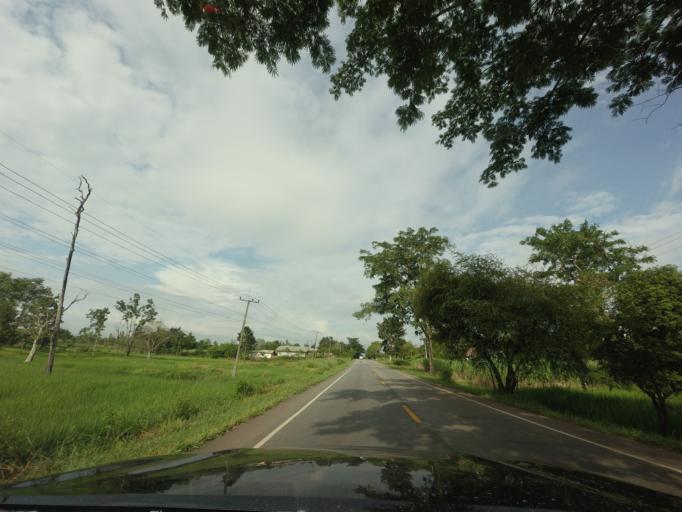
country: TH
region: Changwat Udon Thani
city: Nam Som
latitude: 17.8040
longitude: 102.3047
